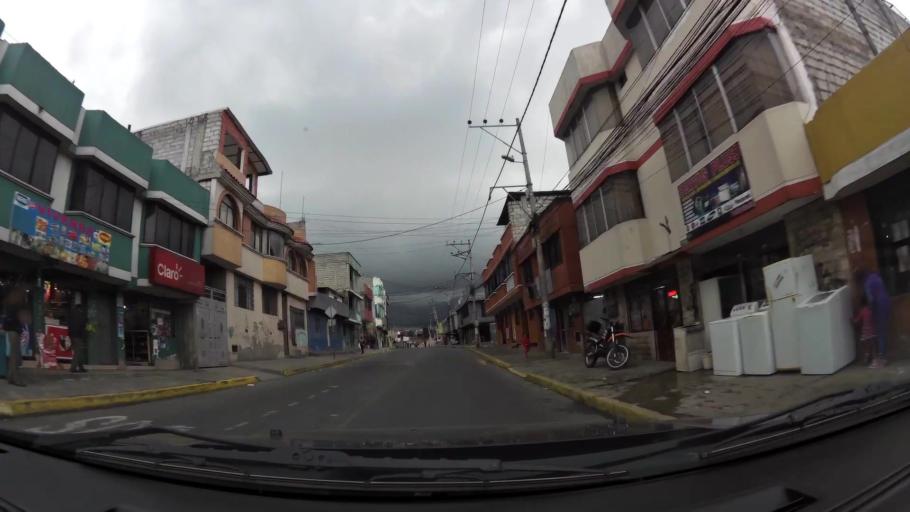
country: EC
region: Pichincha
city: Sangolqui
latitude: -0.3276
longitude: -78.5484
